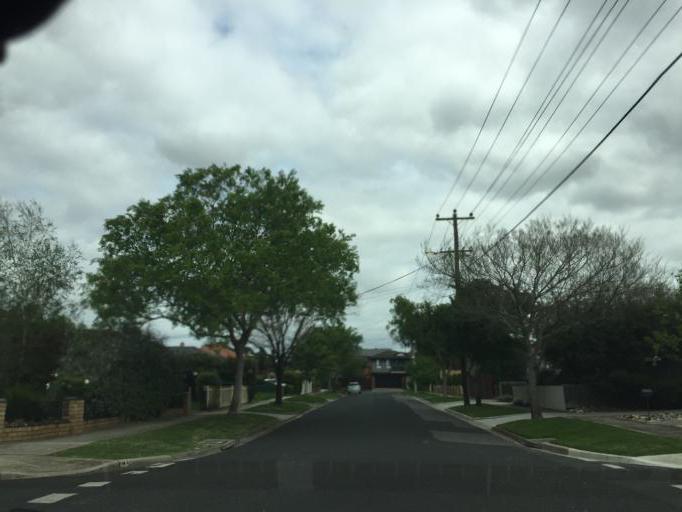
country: AU
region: Victoria
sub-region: Maribyrnong
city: Kingsville
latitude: -37.8144
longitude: 144.8649
